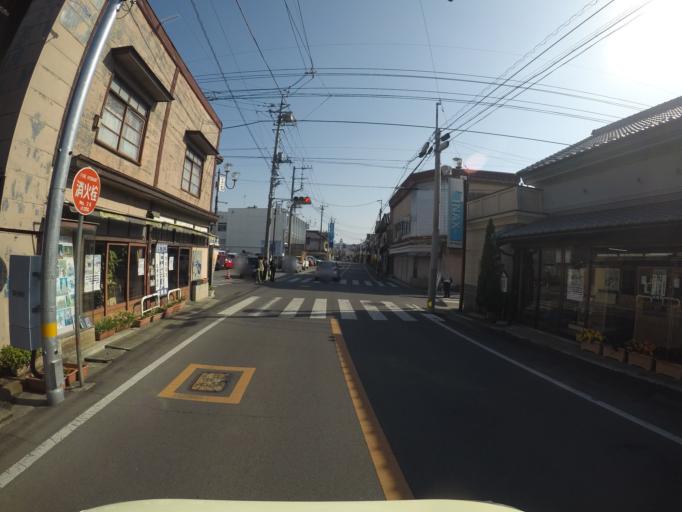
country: JP
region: Ibaraki
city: Yuki
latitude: 36.3034
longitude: 139.8745
